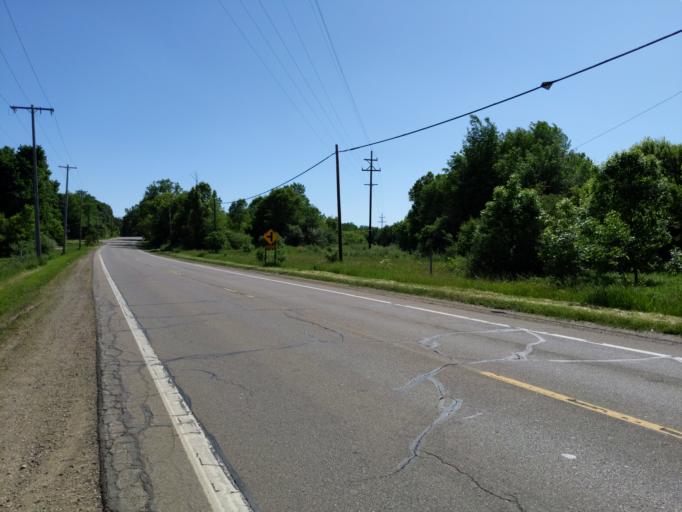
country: US
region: Michigan
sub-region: Jackson County
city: Jackson
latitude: 42.2860
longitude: -84.4005
